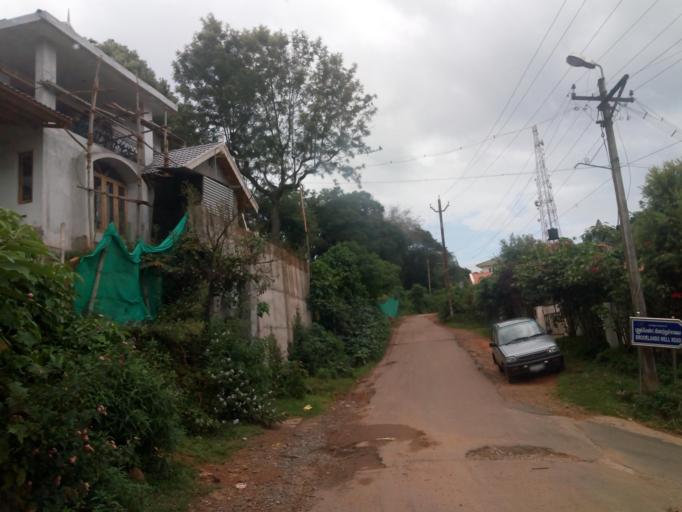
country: IN
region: Tamil Nadu
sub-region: Nilgiri
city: Wellington
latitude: 11.3522
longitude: 76.8103
